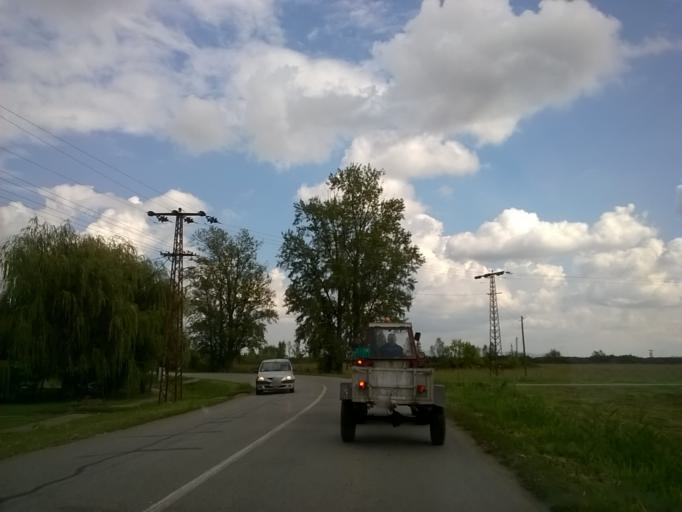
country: RS
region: Autonomna Pokrajina Vojvodina
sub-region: Juznobanatski Okrug
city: Plandiste
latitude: 45.2282
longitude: 21.1337
